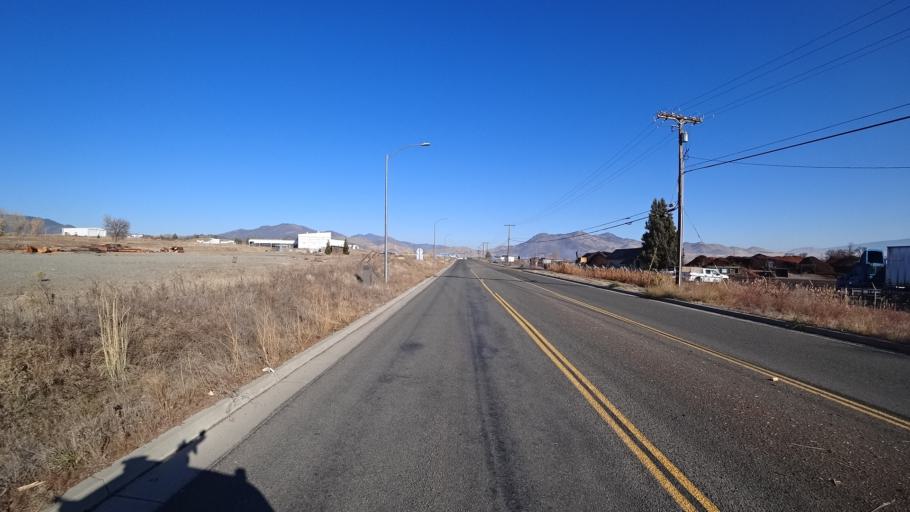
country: US
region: California
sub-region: Siskiyou County
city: Yreka
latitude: 41.7319
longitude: -122.5934
